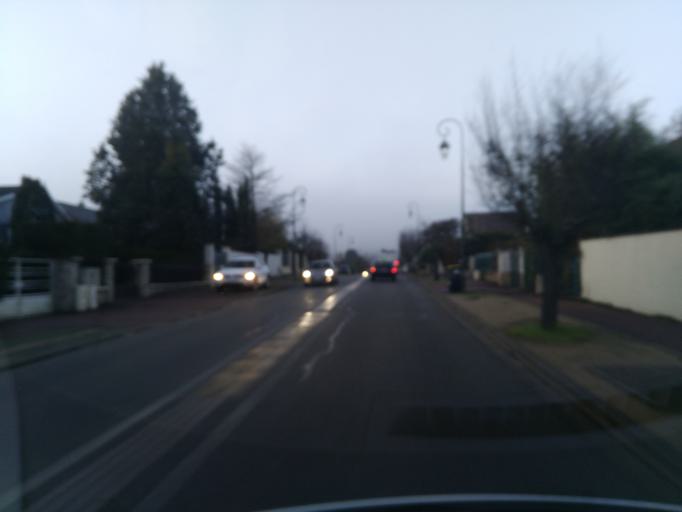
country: FR
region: Ile-de-France
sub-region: Departement des Yvelines
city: Orgeval
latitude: 48.9269
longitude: 1.9793
